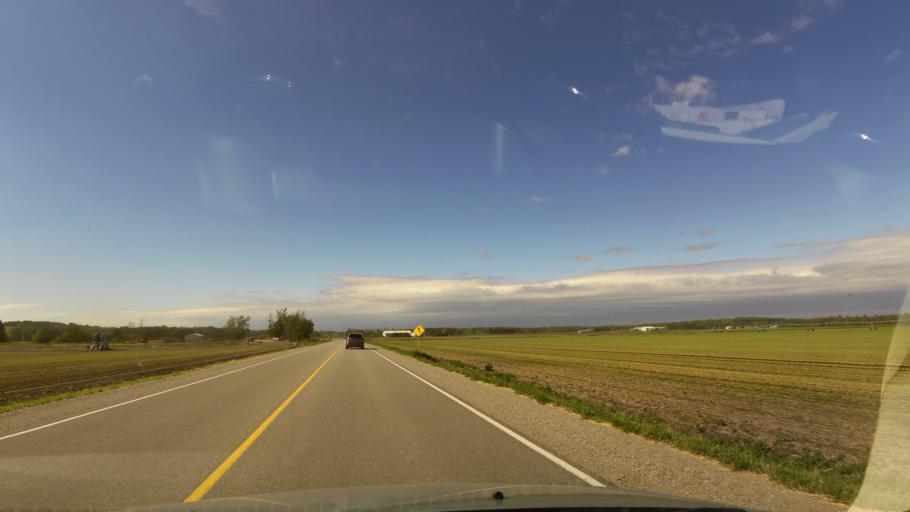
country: CA
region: Ontario
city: Innisfil
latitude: 44.2225
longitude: -79.6322
